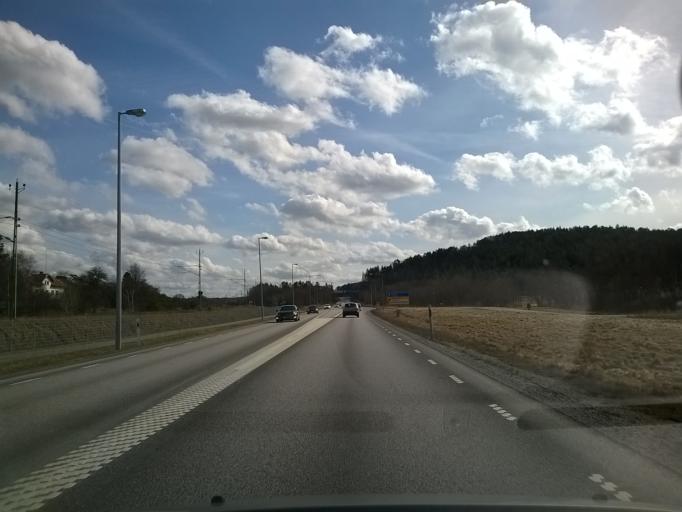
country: SE
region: Vaestra Goetaland
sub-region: Stenungsunds Kommun
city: Stora Hoga
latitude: 58.0329
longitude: 11.8274
